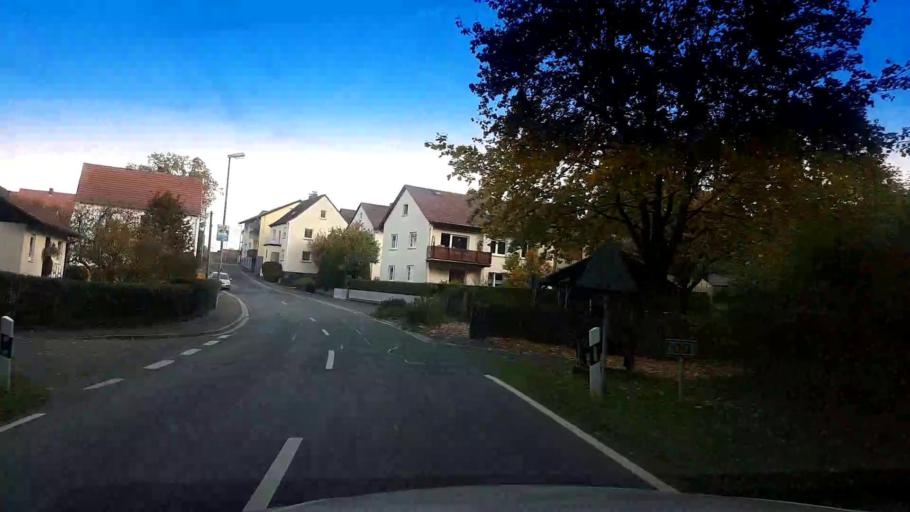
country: DE
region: Bavaria
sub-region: Upper Franconia
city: Altenkunstadt
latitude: 50.1048
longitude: 11.2544
